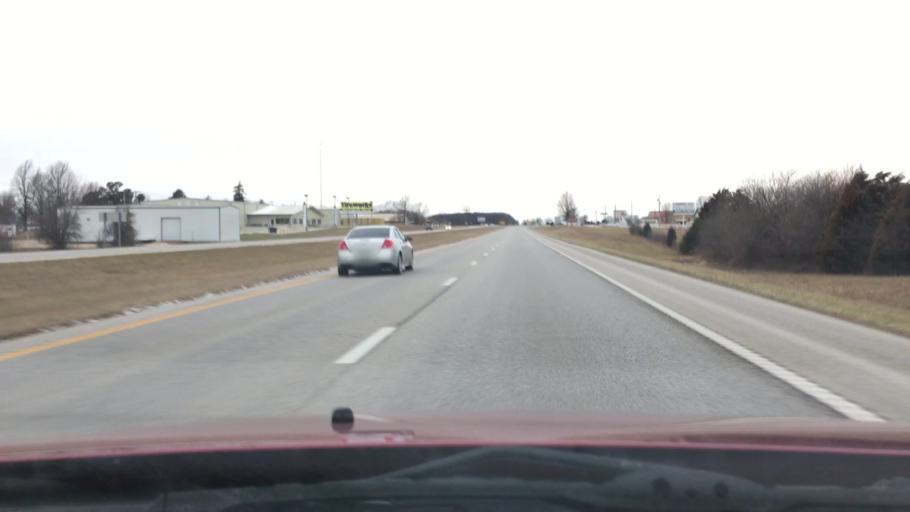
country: US
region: Missouri
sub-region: Webster County
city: Seymour
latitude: 37.1566
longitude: -92.7770
